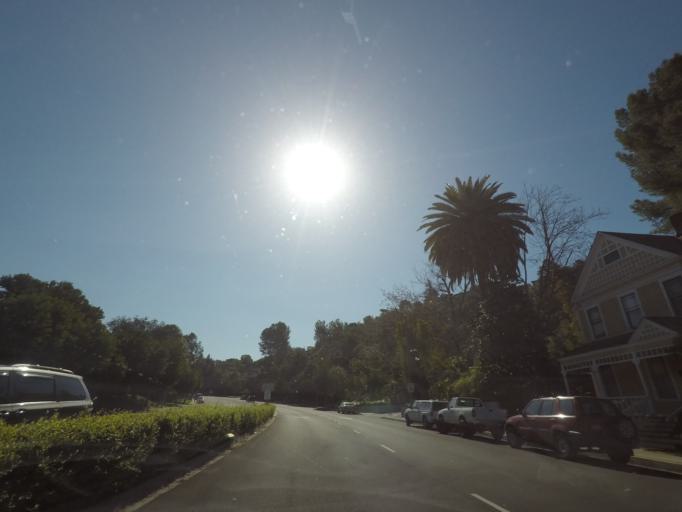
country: US
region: California
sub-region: Los Angeles County
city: South Pasadena
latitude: 34.1116
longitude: -118.1694
